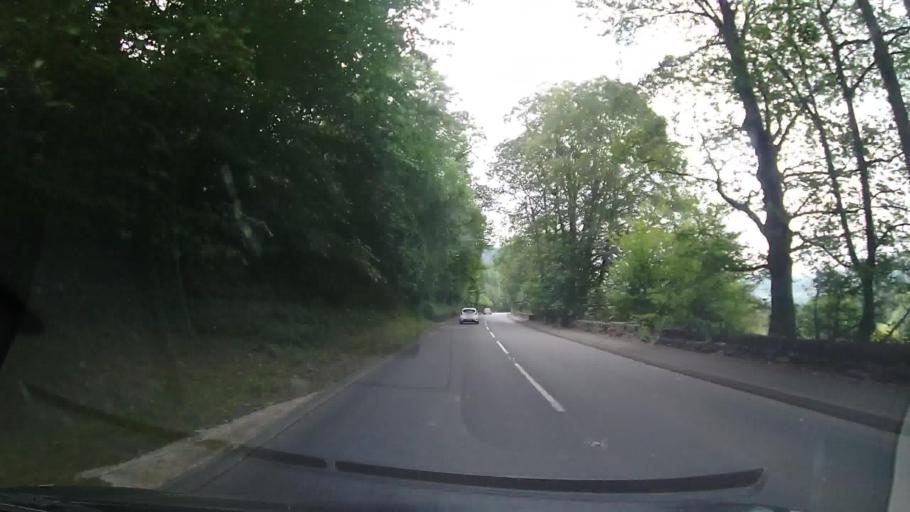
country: GB
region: Wales
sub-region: Wrexham
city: Chirk
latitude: 52.9603
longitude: -3.1039
